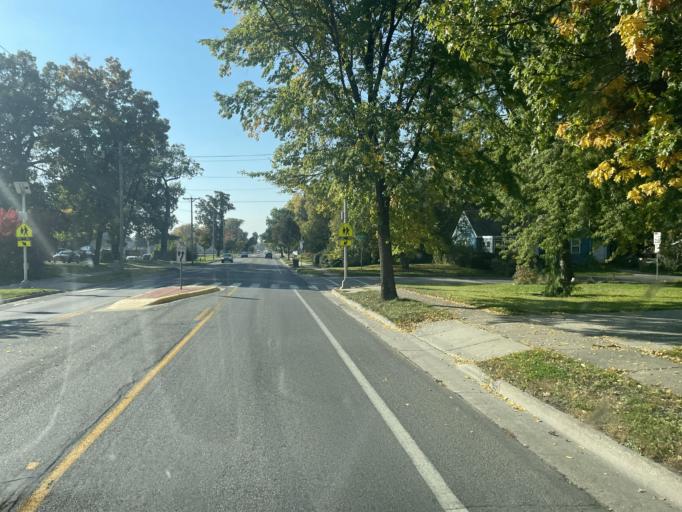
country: US
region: Wisconsin
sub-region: Dane County
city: Maple Bluff
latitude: 43.1180
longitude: -89.3638
